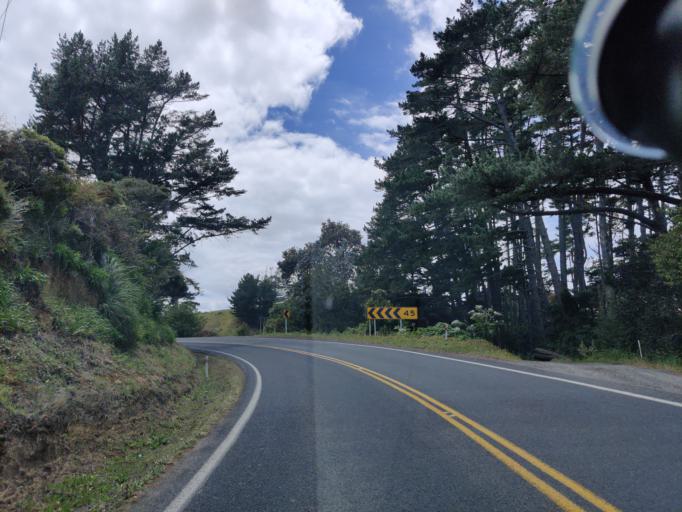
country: NZ
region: Northland
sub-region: Far North District
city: Kaitaia
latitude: -34.9968
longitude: 173.1941
